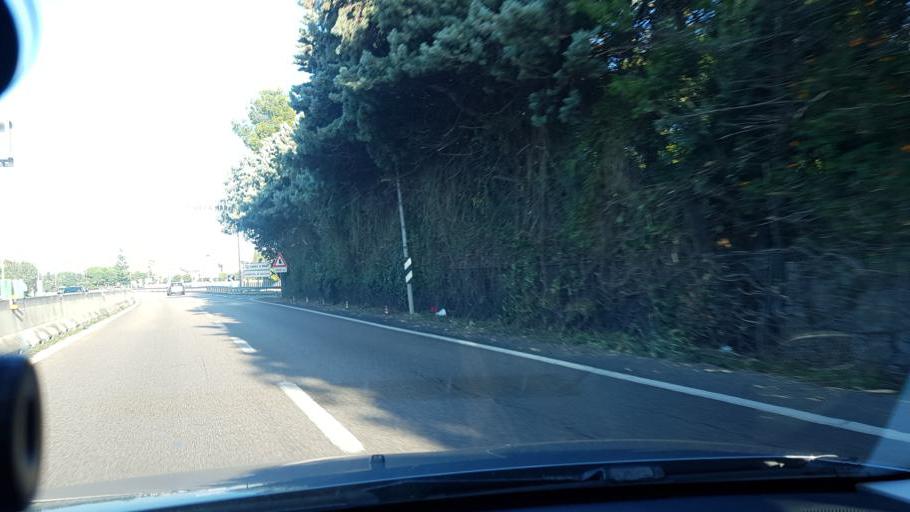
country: IT
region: Apulia
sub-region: Provincia di Bari
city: Parco Scizzo-Parchitello
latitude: 41.0861
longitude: 16.9900
